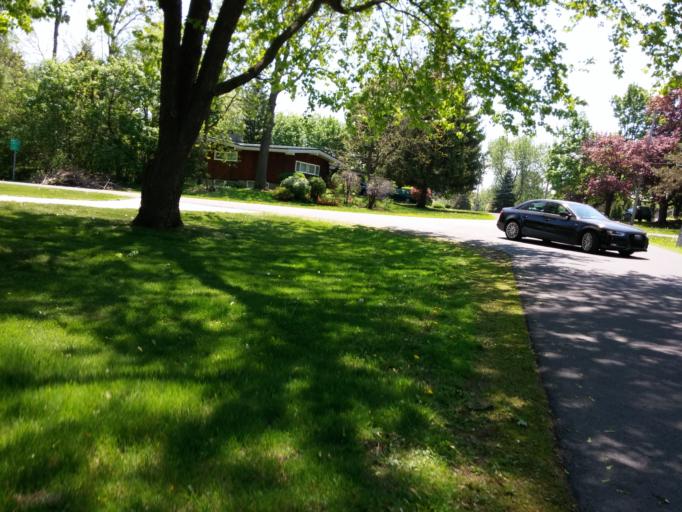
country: CA
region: Quebec
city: Baie-D'Urfe
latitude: 45.4213
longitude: -73.8998
